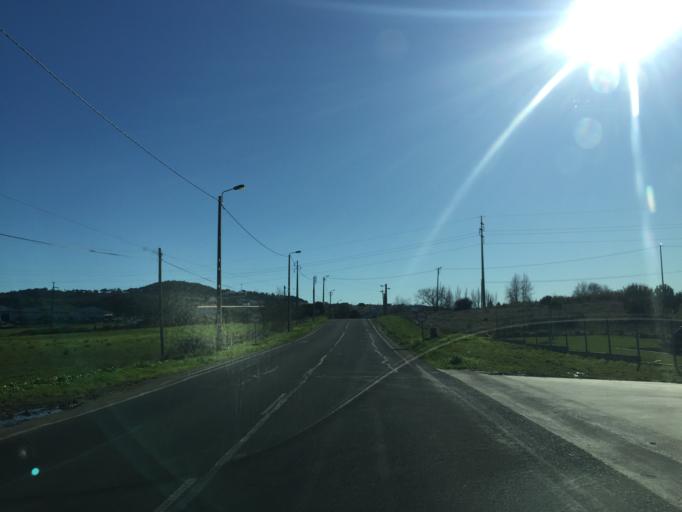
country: PT
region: Lisbon
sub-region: Sintra
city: Pero Pinheiro
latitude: 38.8321
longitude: -9.3063
